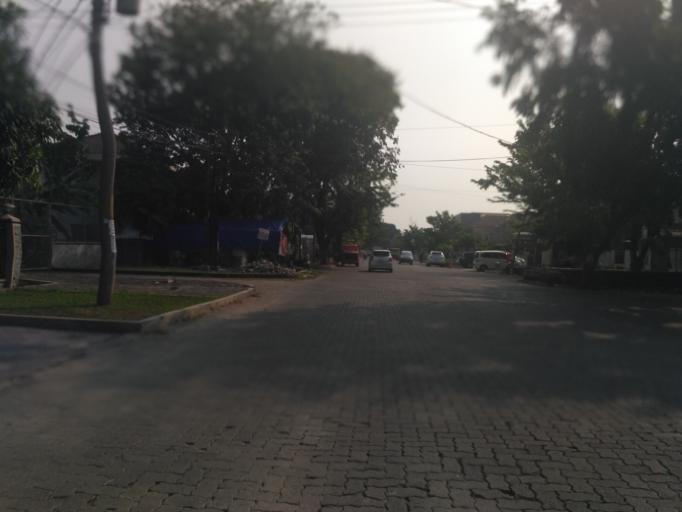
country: ID
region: Central Java
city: Semarang
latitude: -6.9678
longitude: 110.3890
